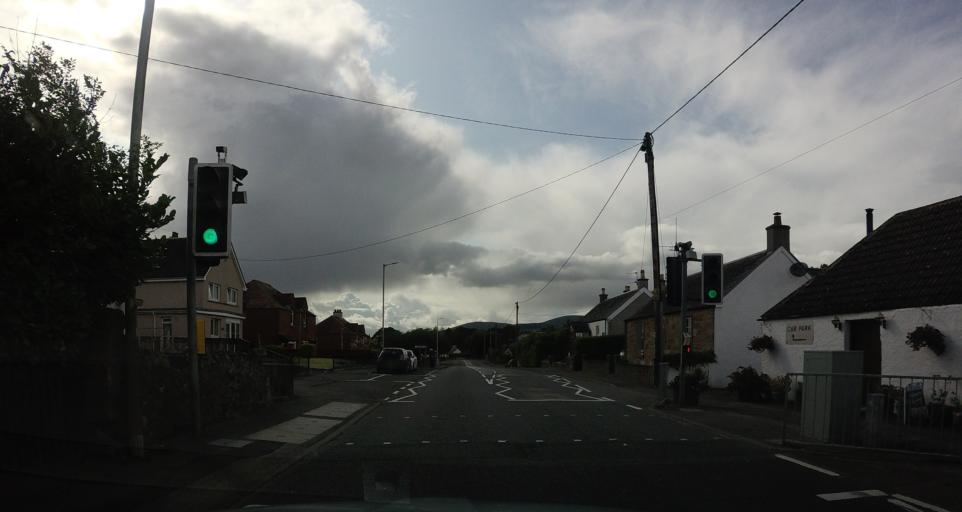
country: GB
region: Scotland
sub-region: Fife
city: Saline
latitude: 56.1847
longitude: -3.5563
